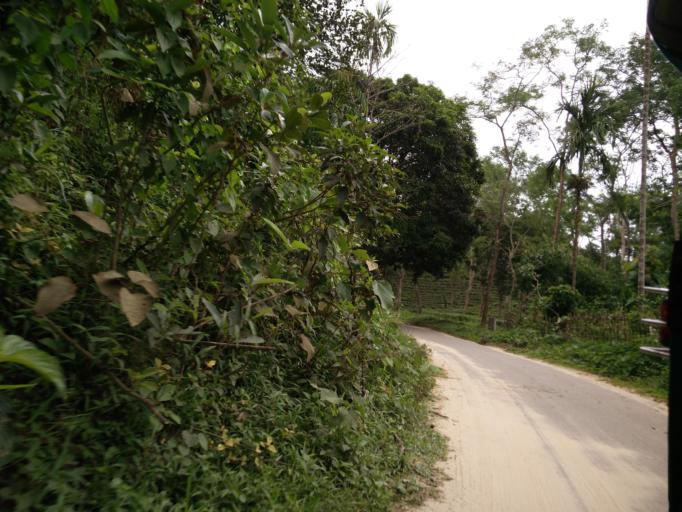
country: IN
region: Tripura
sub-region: Dhalai
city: Kamalpur
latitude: 24.3025
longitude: 91.7881
